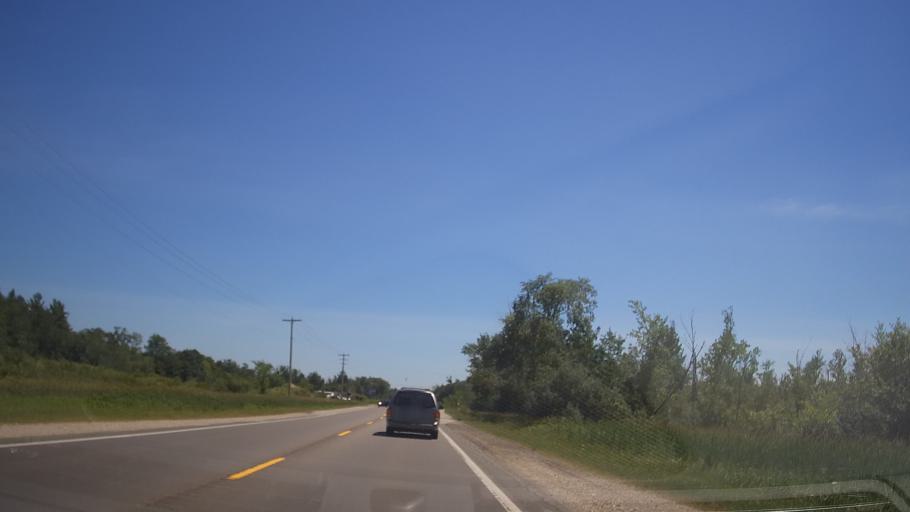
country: US
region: Michigan
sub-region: Wexford County
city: Cadillac
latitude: 44.2545
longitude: -85.4624
